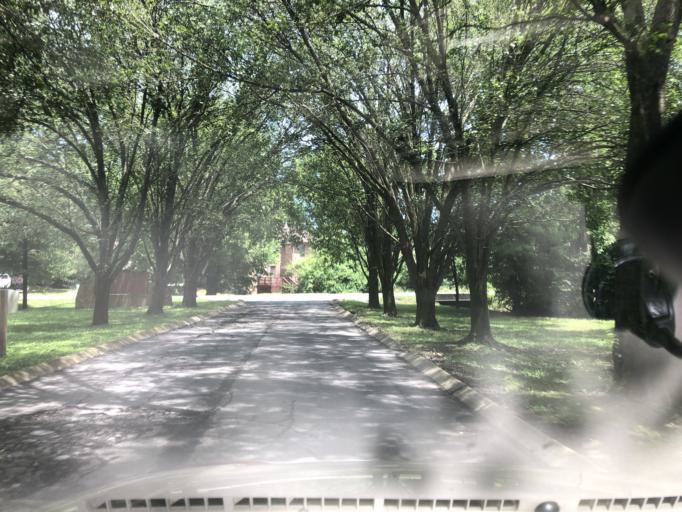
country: US
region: Tennessee
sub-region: Davidson County
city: Goodlettsville
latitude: 36.2578
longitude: -86.7046
